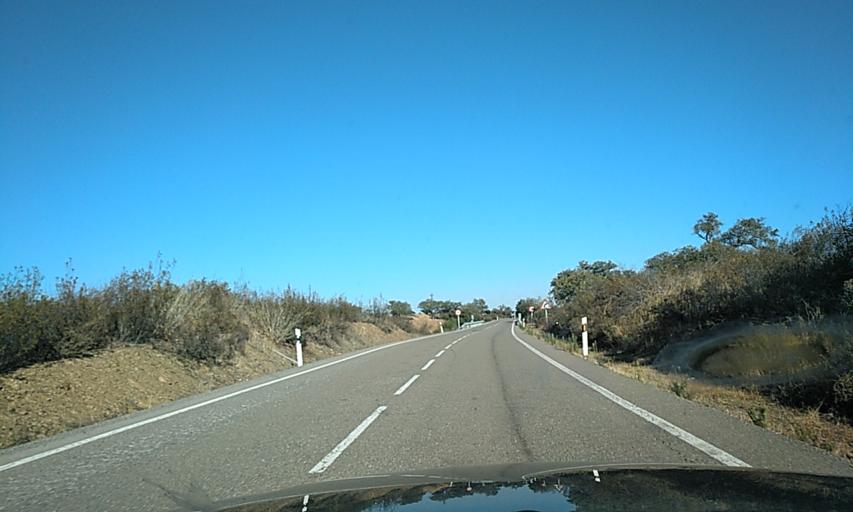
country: ES
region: Andalusia
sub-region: Provincia de Huelva
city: Santa Barbara de Casa
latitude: 37.7808
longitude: -7.1581
